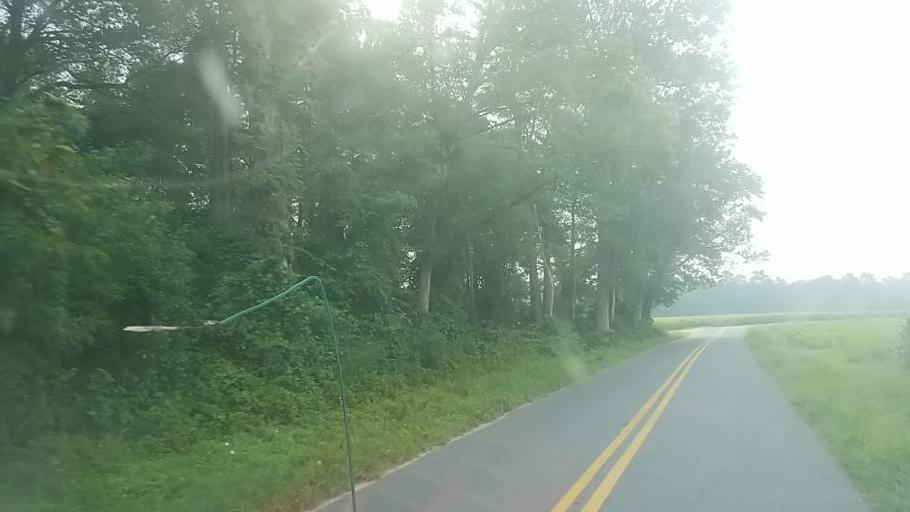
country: US
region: Maryland
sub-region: Wicomico County
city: Pittsville
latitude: 38.4392
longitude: -75.3297
